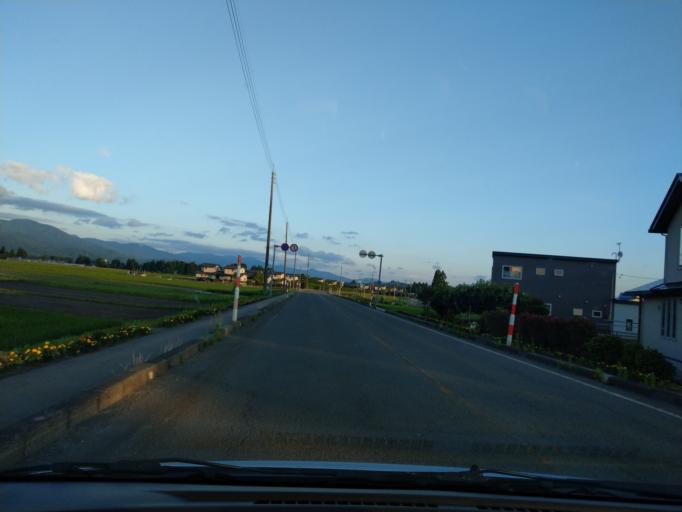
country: JP
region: Akita
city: Kakunodatemachi
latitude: 39.6401
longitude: 140.5721
